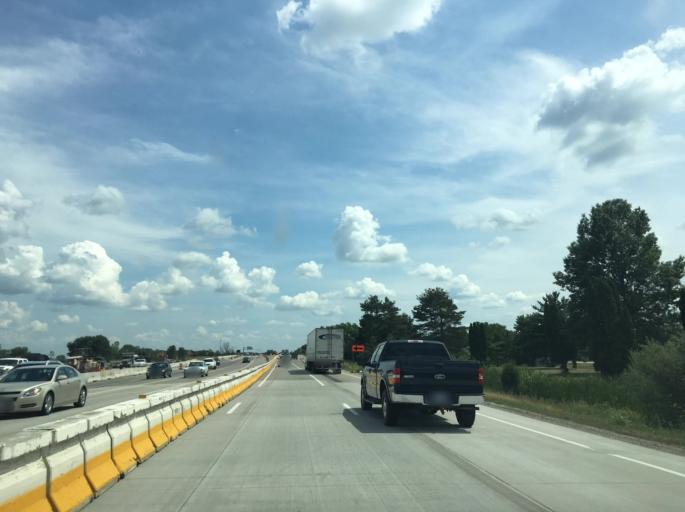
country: US
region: Michigan
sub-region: Saginaw County
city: Bridgeport
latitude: 43.3556
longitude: -83.8665
